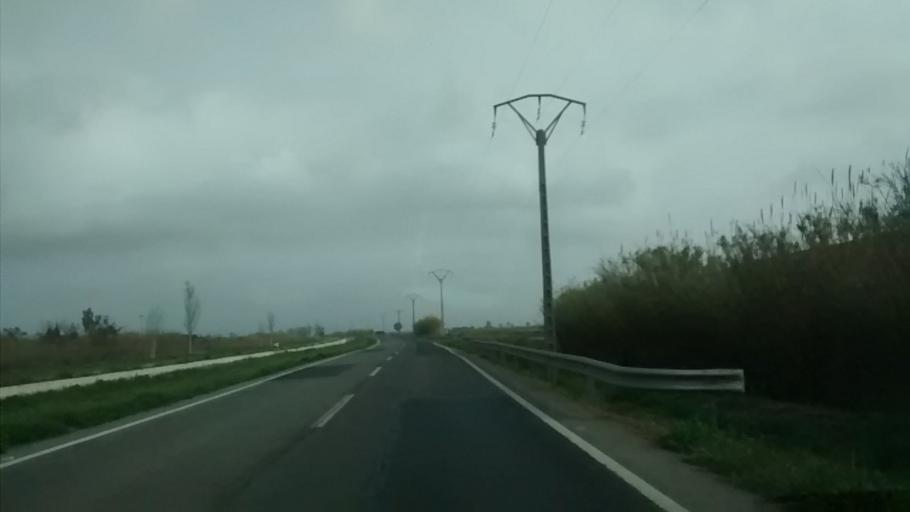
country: ES
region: Catalonia
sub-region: Provincia de Tarragona
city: Sant Carles de la Rapita
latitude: 40.6305
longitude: 0.6011
